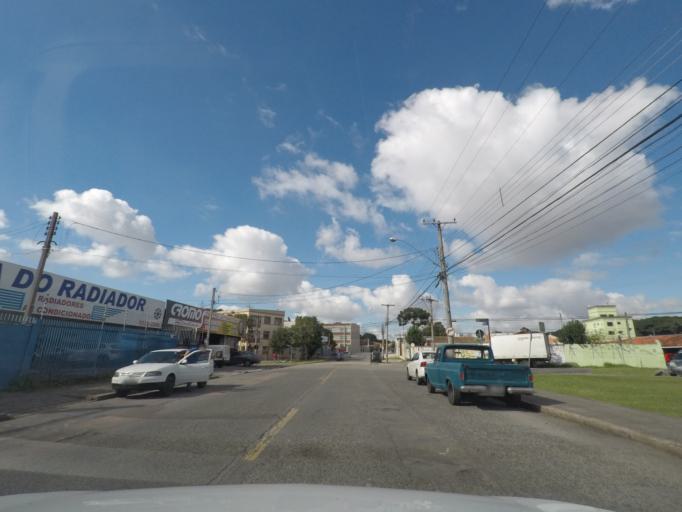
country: BR
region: Parana
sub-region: Curitiba
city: Curitiba
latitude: -25.4477
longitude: -49.2571
